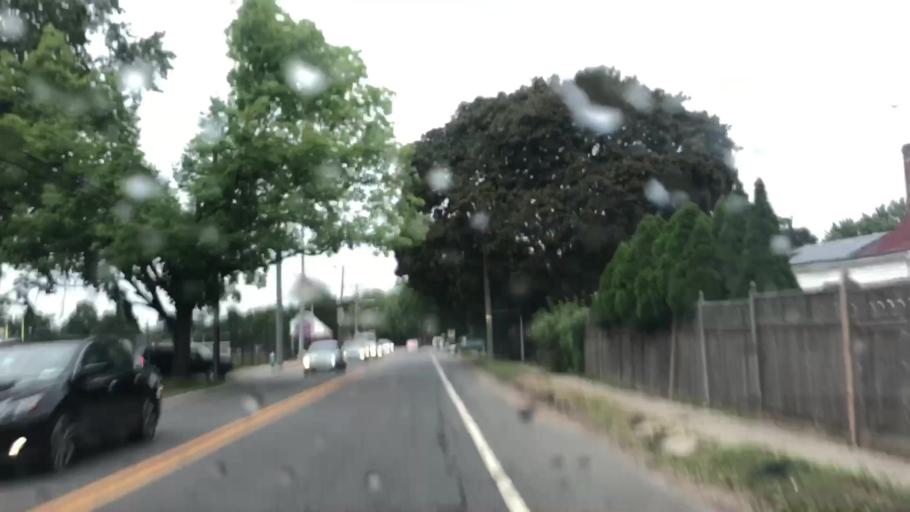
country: US
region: New York
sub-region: Nassau County
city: Stewart Manor
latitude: 40.7137
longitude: -73.6891
